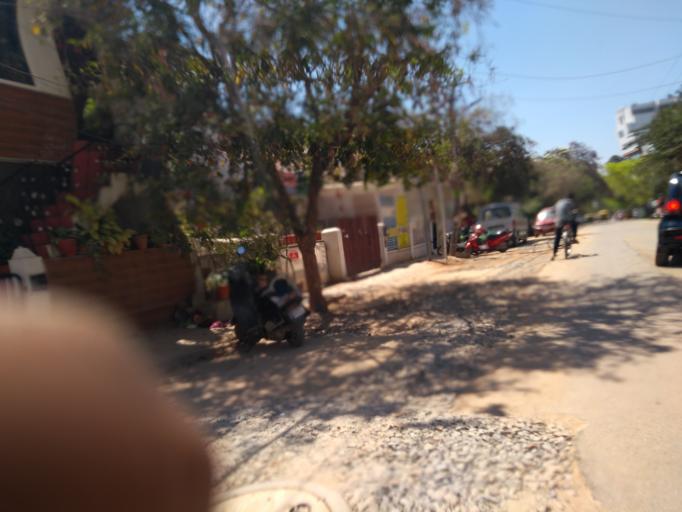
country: IN
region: Karnataka
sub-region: Bangalore Urban
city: Bangalore
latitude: 12.9703
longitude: 77.6542
